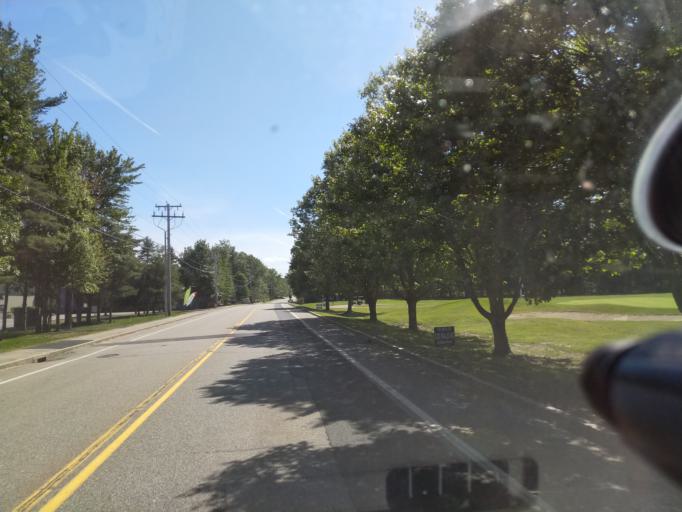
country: US
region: Maine
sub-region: Cumberland County
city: Westbrook
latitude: 43.7104
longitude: -70.3135
